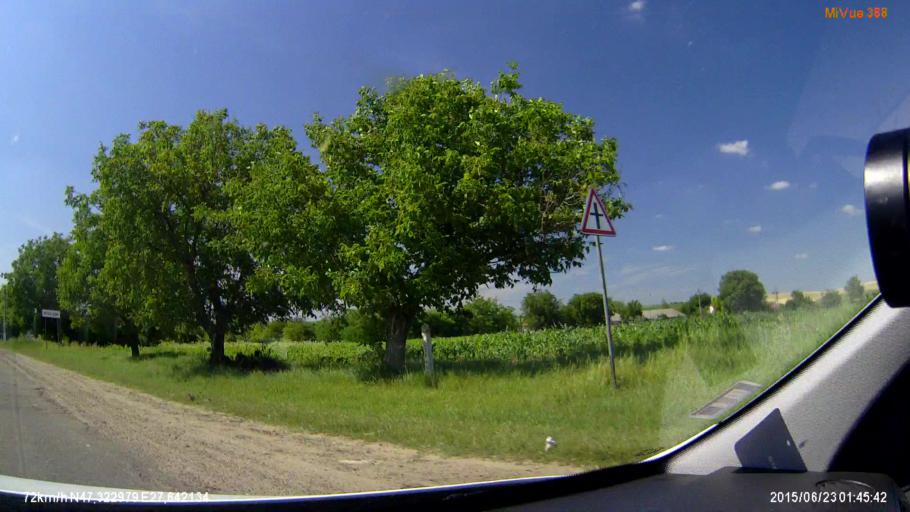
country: RO
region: Iasi
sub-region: Comuna Victoria
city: Victoria
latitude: 47.3229
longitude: 27.6424
